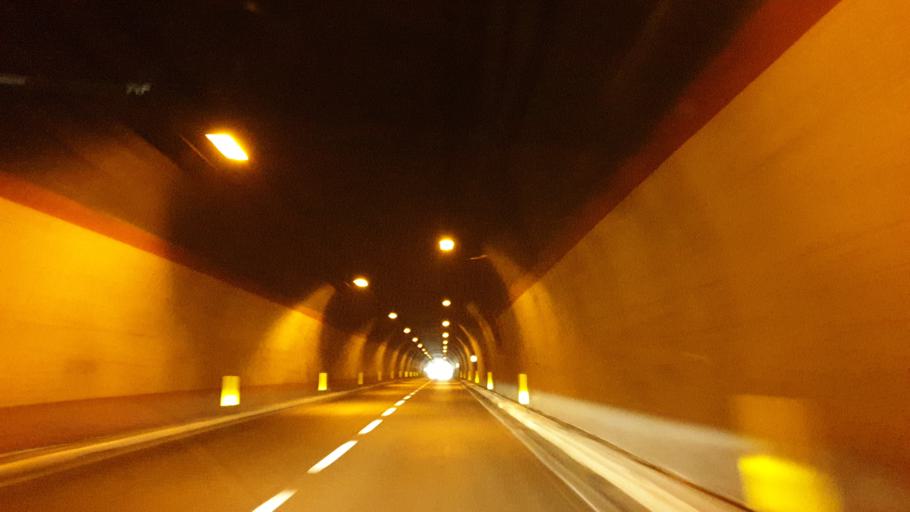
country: IT
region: Emilia-Romagna
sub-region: Forli-Cesena
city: Sarsina
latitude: 43.8923
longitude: 12.0794
